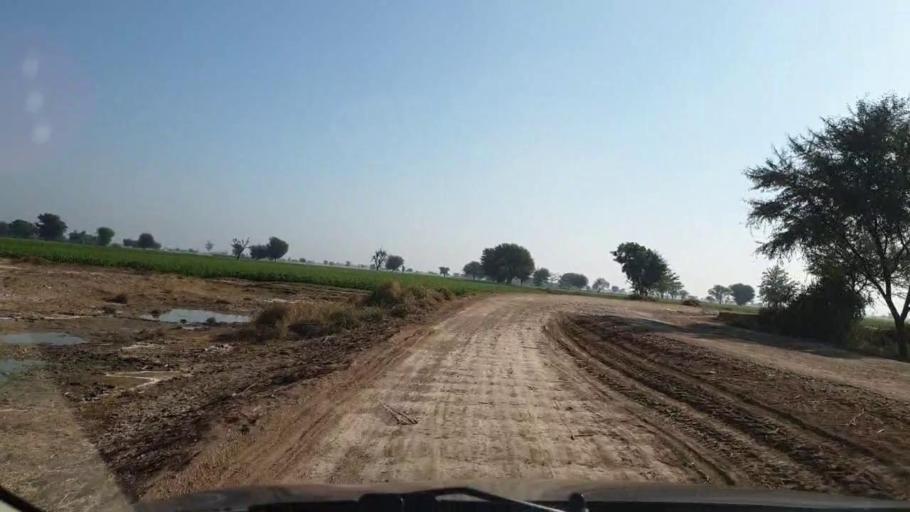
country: PK
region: Sindh
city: Sinjhoro
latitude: 25.9831
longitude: 68.7450
